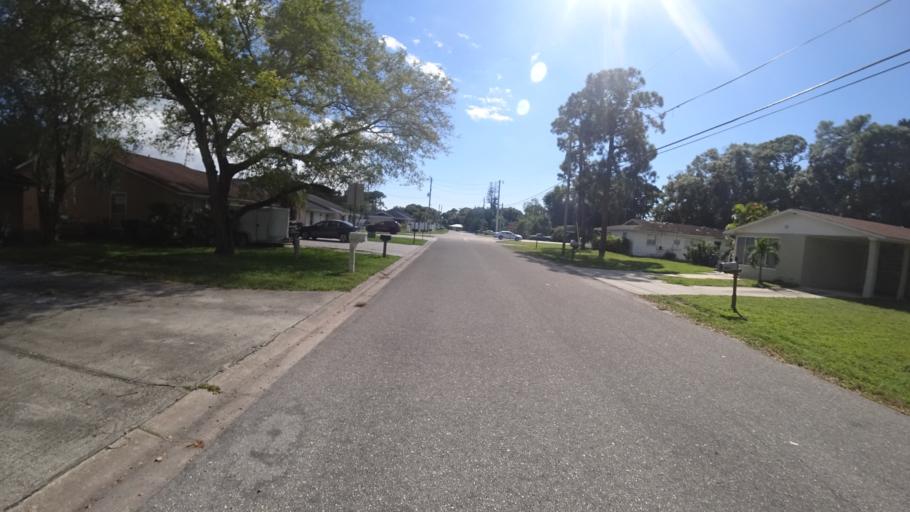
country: US
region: Florida
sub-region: Manatee County
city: South Bradenton
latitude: 27.4742
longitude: -82.5857
